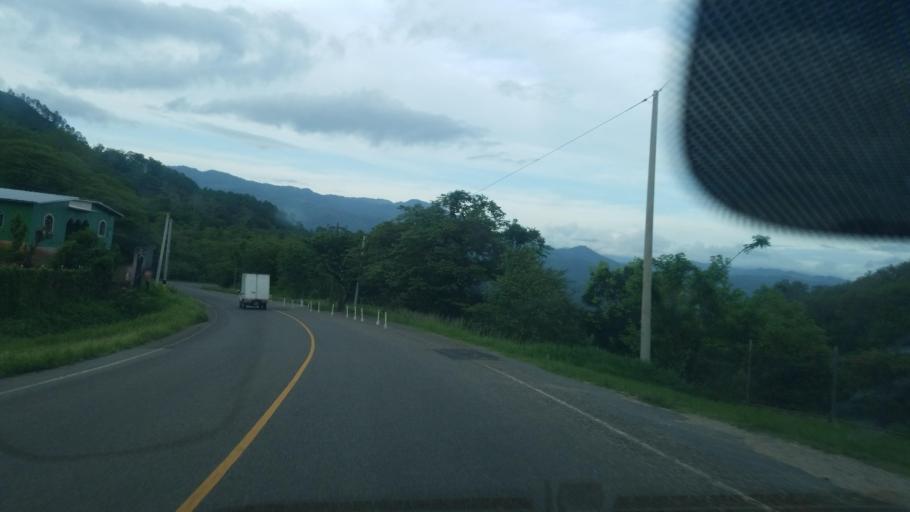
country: HN
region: Santa Barbara
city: Concepcion del Sur
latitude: 14.7954
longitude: -88.1640
